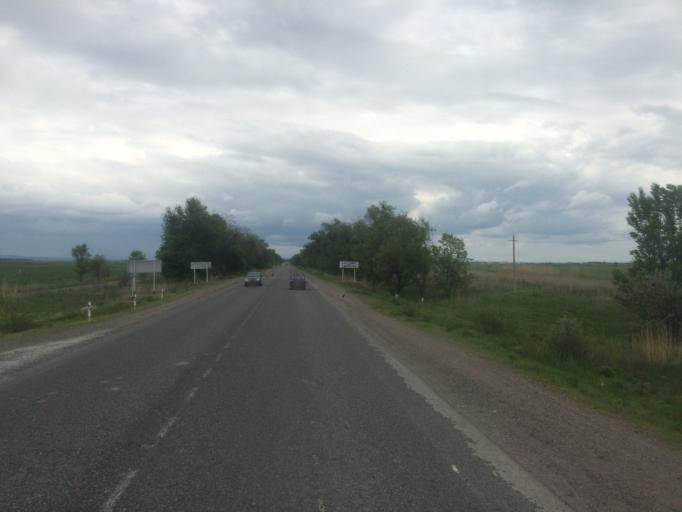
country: KZ
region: Zhambyl
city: Georgiyevka
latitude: 43.2262
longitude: 74.4063
